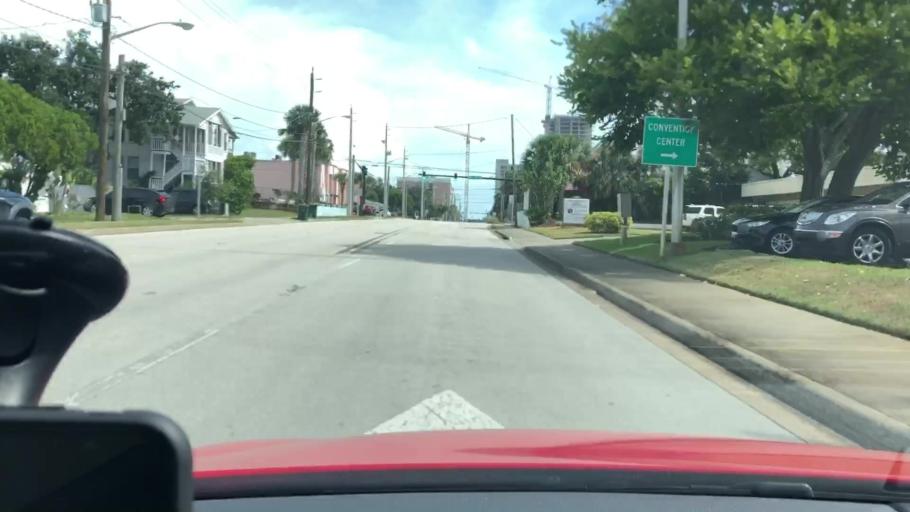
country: US
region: Florida
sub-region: Volusia County
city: Daytona Beach
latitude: 29.2319
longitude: -81.0169
